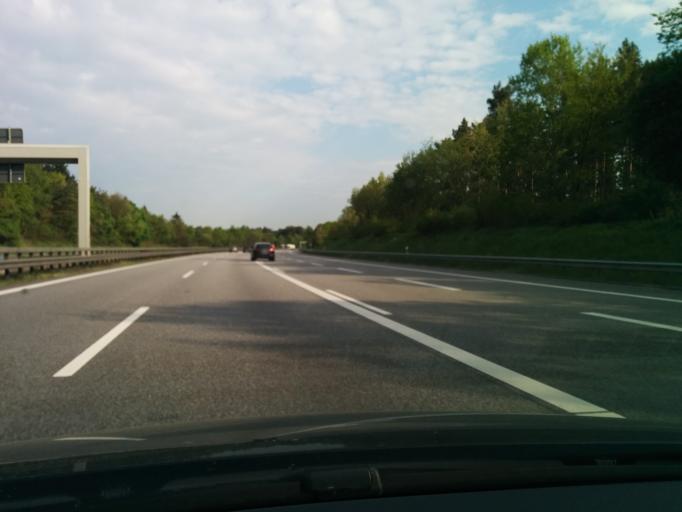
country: DE
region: Lower Saxony
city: Seevetal
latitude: 53.4401
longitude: 9.9212
